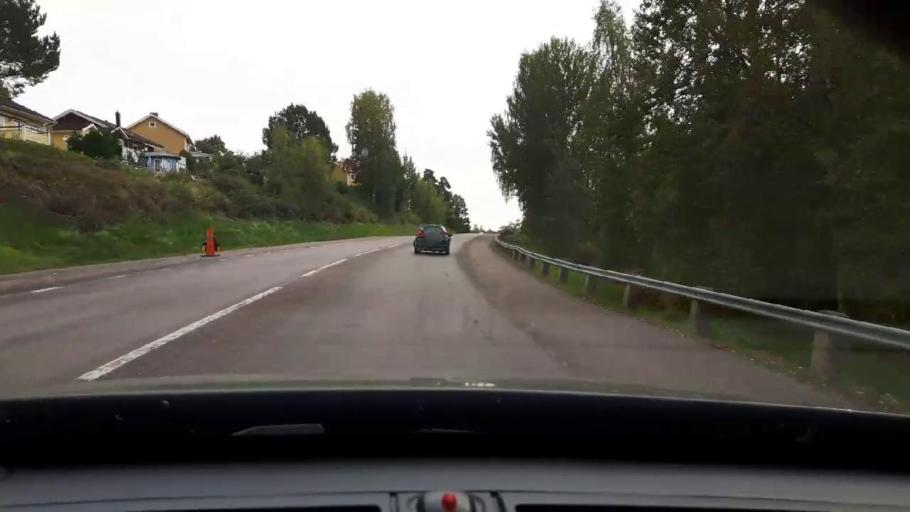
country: SE
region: Dalarna
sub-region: Ludvika Kommun
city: Ludvika
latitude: 60.1605
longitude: 15.1825
